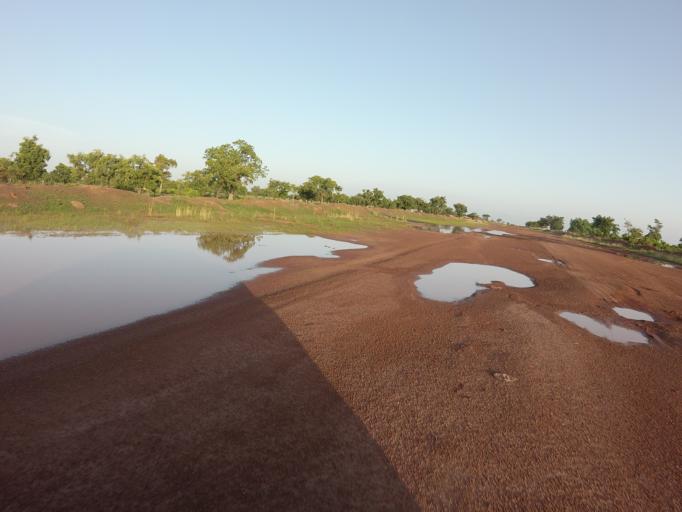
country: TG
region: Savanes
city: Sansanne-Mango
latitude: 10.2328
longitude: -0.0730
